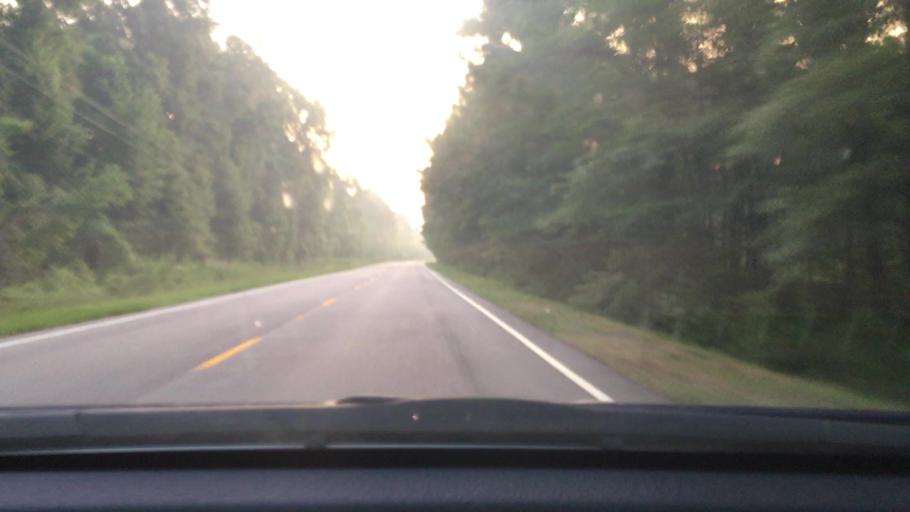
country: US
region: South Carolina
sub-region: Lee County
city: Bishopville
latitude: 34.1233
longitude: -80.1392
